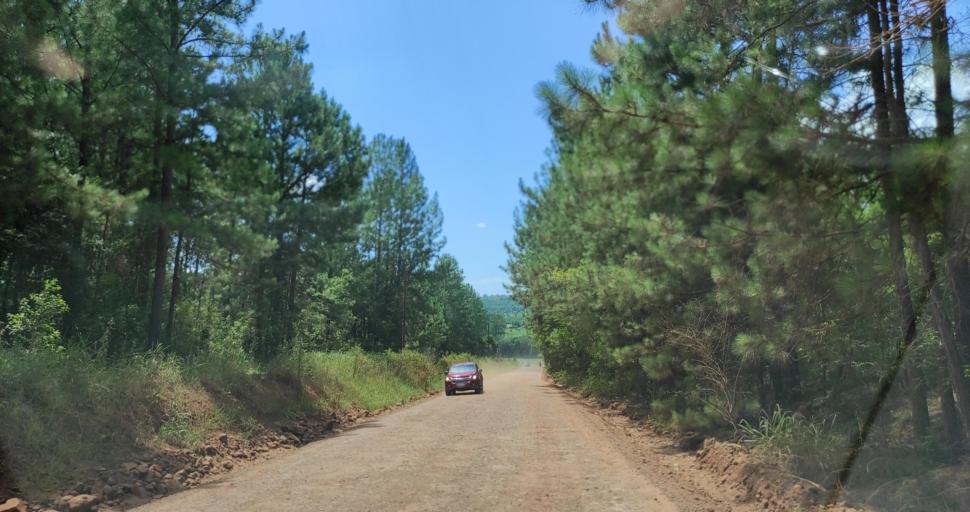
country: AR
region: Misiones
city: Ruiz de Montoya
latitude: -27.0426
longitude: -55.0070
